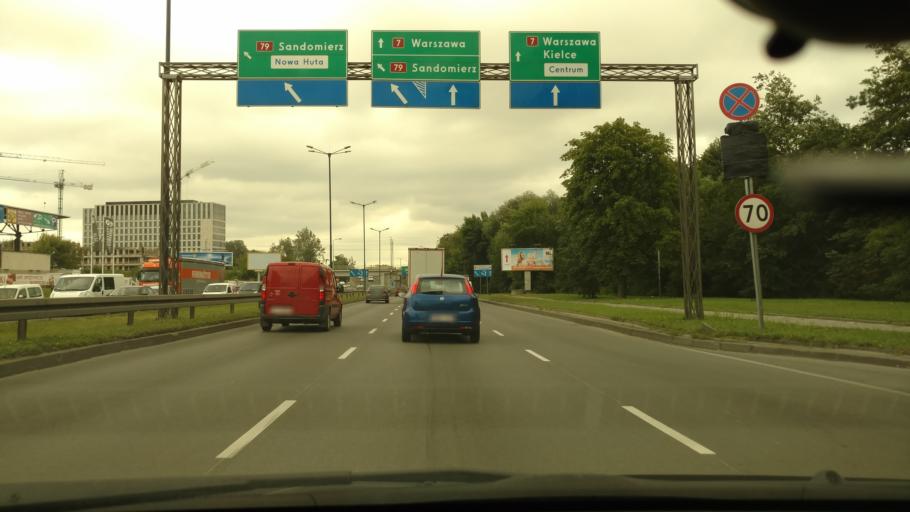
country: PL
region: Lesser Poland Voivodeship
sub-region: Krakow
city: Krakow
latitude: 50.0875
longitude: 19.9486
